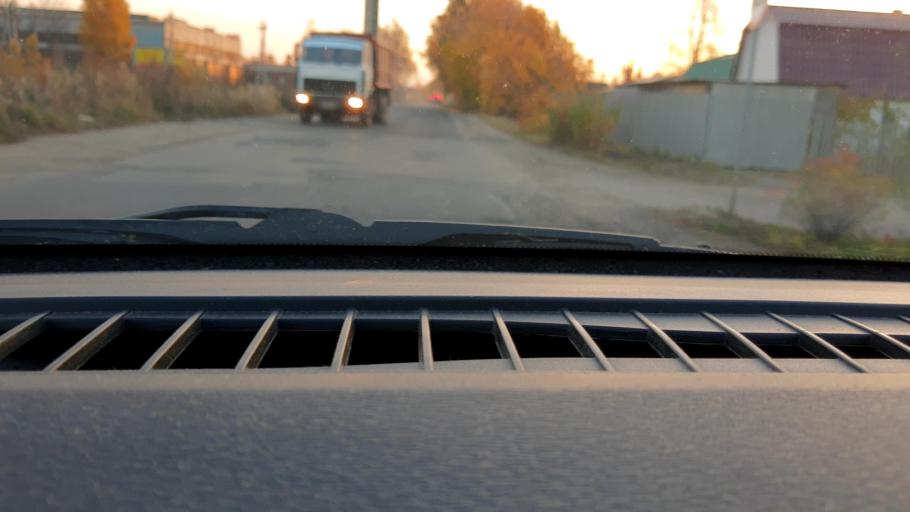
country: RU
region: Nizjnij Novgorod
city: Kstovo
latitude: 56.1857
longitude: 44.1513
